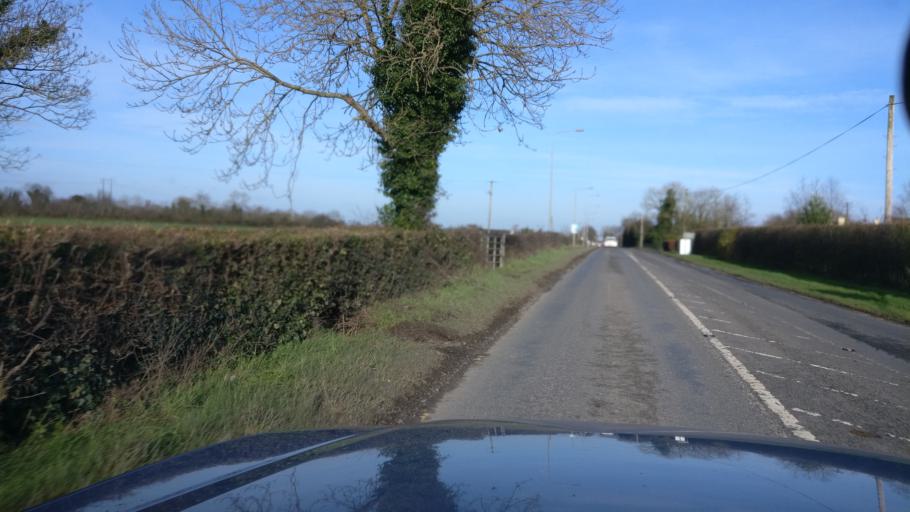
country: IE
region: Leinster
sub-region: Laois
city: Portlaoise
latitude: 53.0263
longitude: -7.2664
